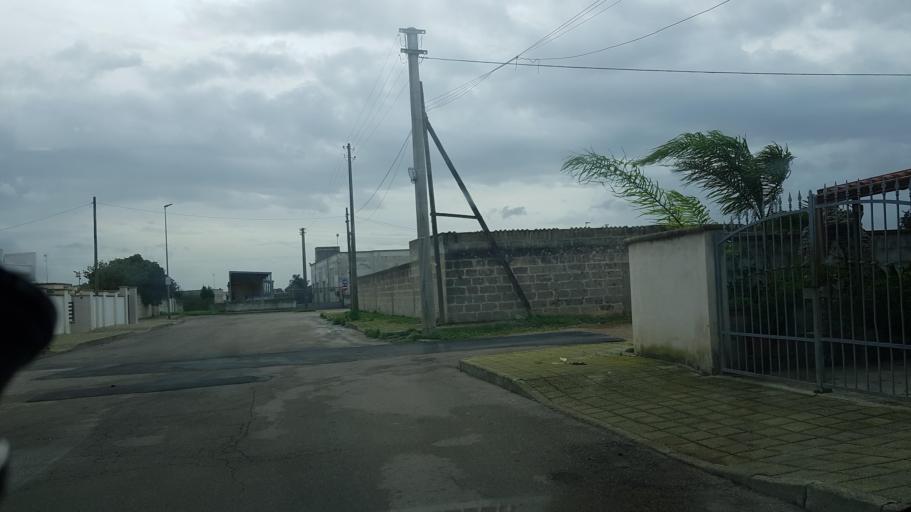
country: IT
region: Apulia
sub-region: Provincia di Lecce
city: Carmiano
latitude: 40.3447
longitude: 18.0338
